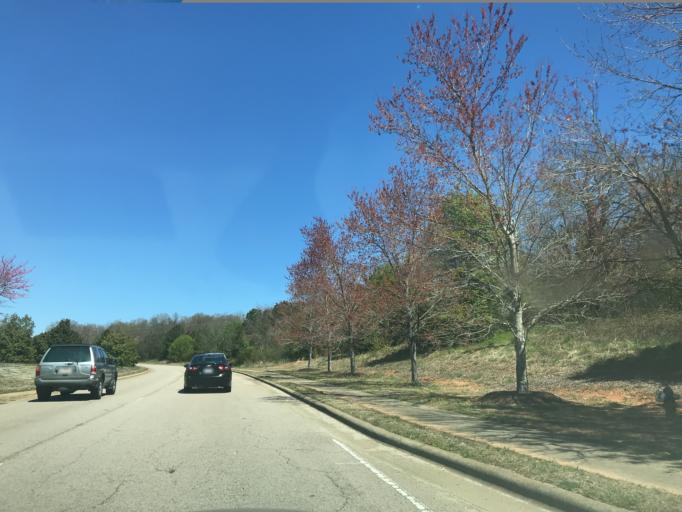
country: US
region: North Carolina
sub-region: Wake County
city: West Raleigh
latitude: 35.7709
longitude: -78.6690
